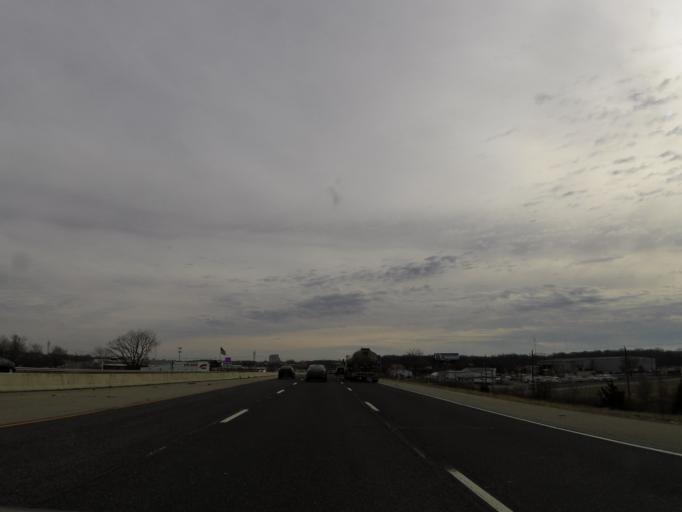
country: US
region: Indiana
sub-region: Boone County
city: Zionsville
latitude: 39.9251
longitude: -86.2498
